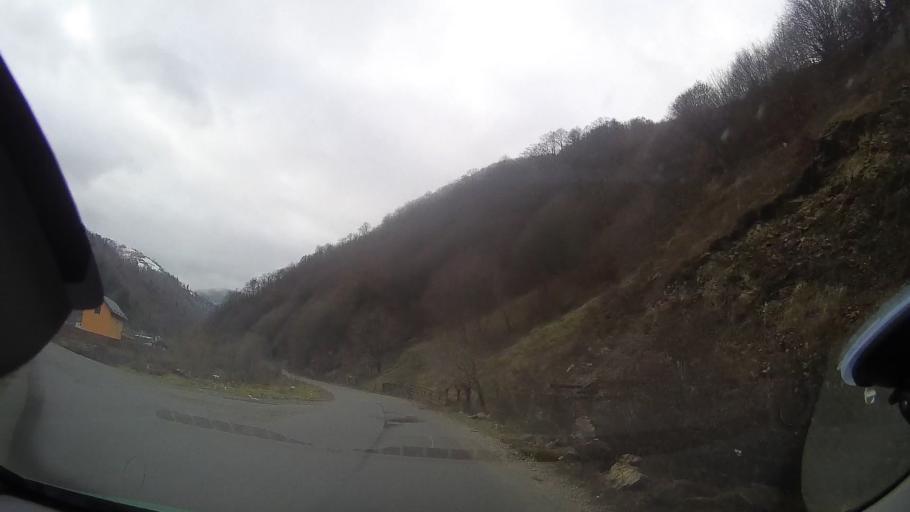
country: RO
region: Cluj
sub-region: Comuna Maguri-Racatau
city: Maguri-Racatau
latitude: 46.6452
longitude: 23.1937
